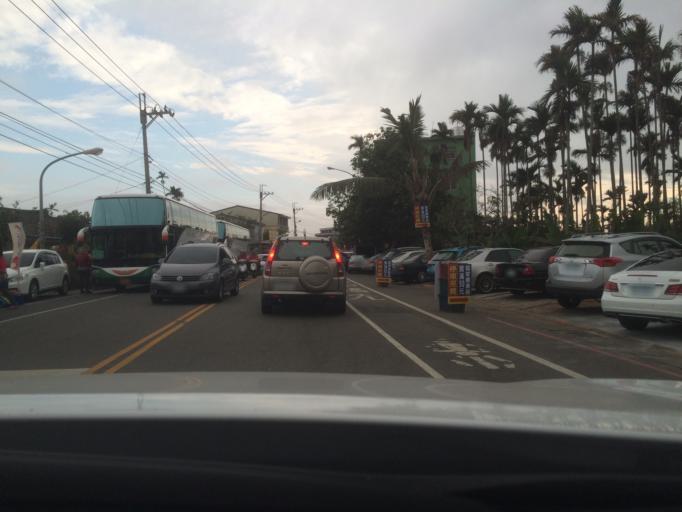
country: TW
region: Taiwan
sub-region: Nantou
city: Nantou
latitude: 23.9357
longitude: 120.6381
